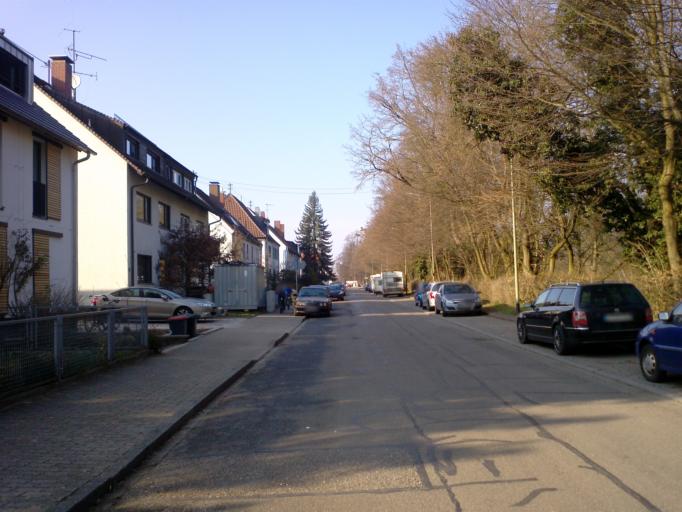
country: DE
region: Baden-Wuerttemberg
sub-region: Karlsruhe Region
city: Karlsruhe
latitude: 48.9821
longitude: 8.3965
